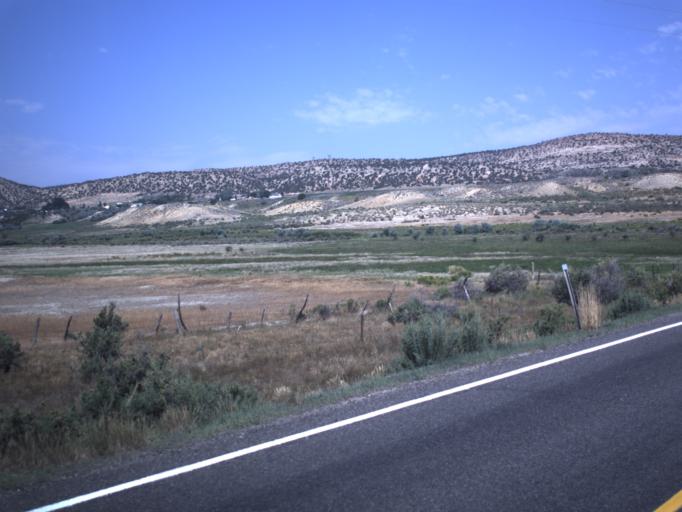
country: US
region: Utah
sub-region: Daggett County
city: Manila
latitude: 40.9760
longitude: -109.7221
